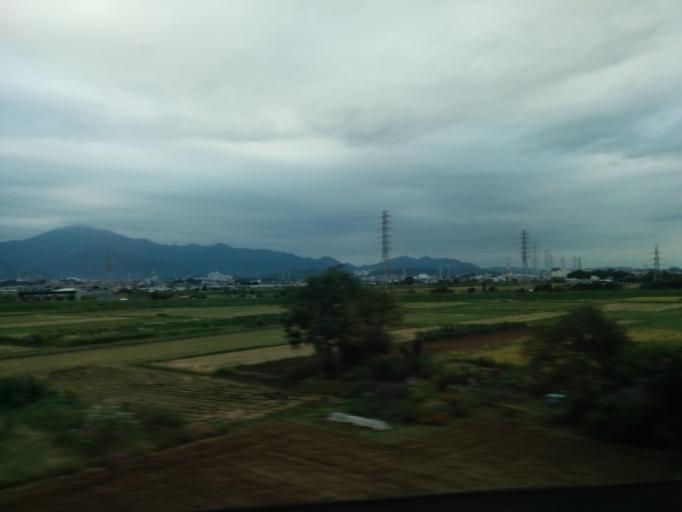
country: JP
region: Kanagawa
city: Isehara
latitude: 35.3780
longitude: 139.3515
